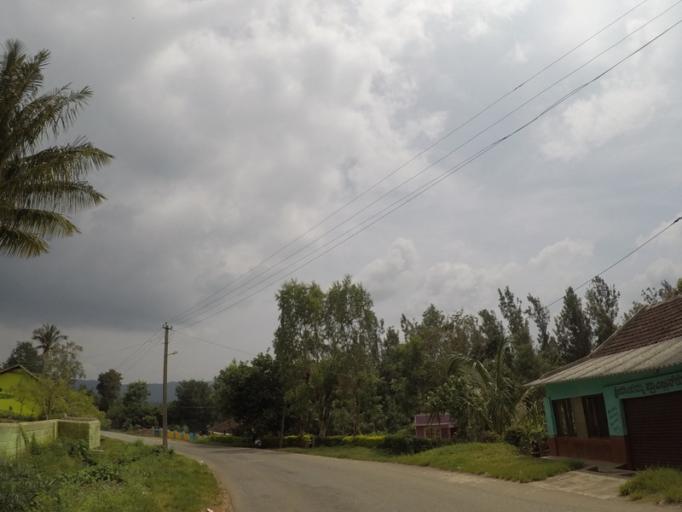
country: IN
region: Karnataka
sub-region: Chikmagalur
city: Chikmagalur
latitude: 13.4417
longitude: 75.8032
